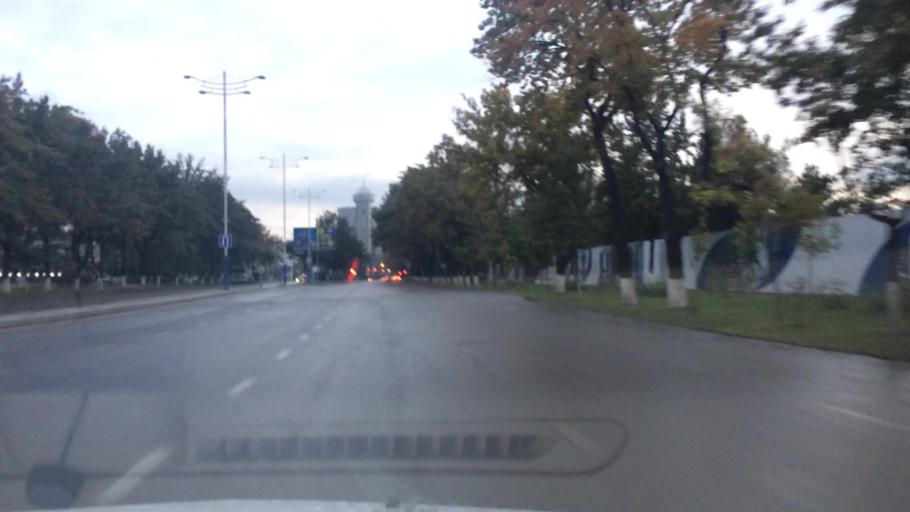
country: UZ
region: Toshkent Shahri
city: Tashkent
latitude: 41.3117
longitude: 69.2468
